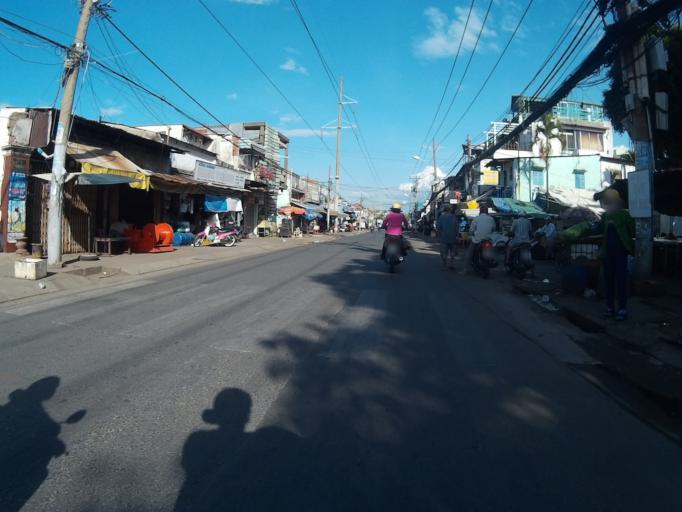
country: VN
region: Ho Chi Minh City
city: Quan Bon
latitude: 10.7514
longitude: 106.6931
